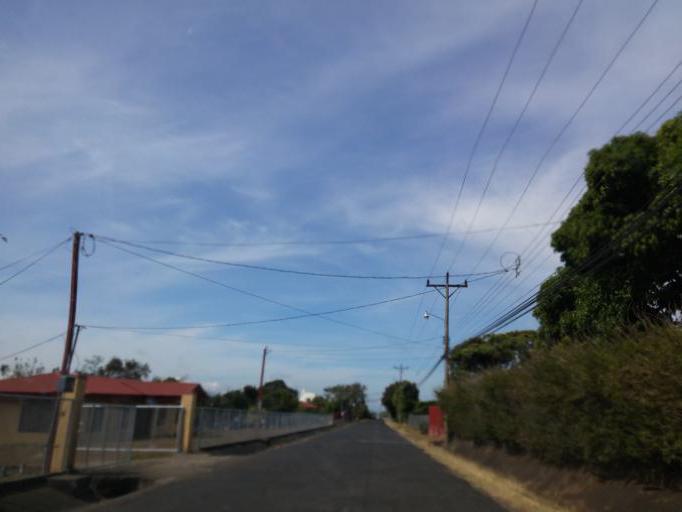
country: CR
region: Alajuela
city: Sabanilla
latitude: 10.0474
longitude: -84.2223
